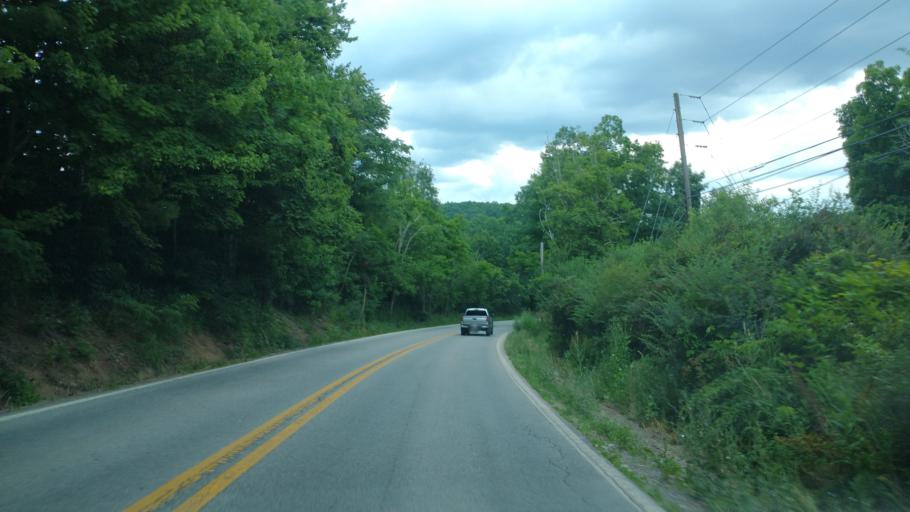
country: US
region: West Virginia
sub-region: Mercer County
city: Athens
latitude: 37.4469
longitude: -81.0016
